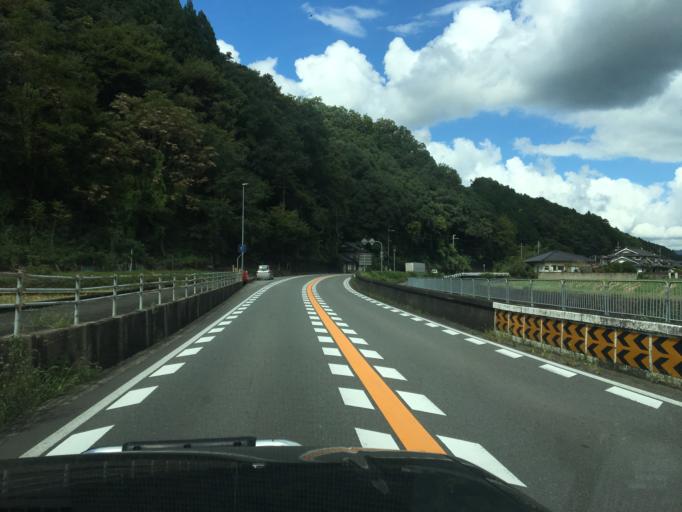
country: JP
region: Kyoto
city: Fukuchiyama
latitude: 35.3178
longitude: 134.8900
